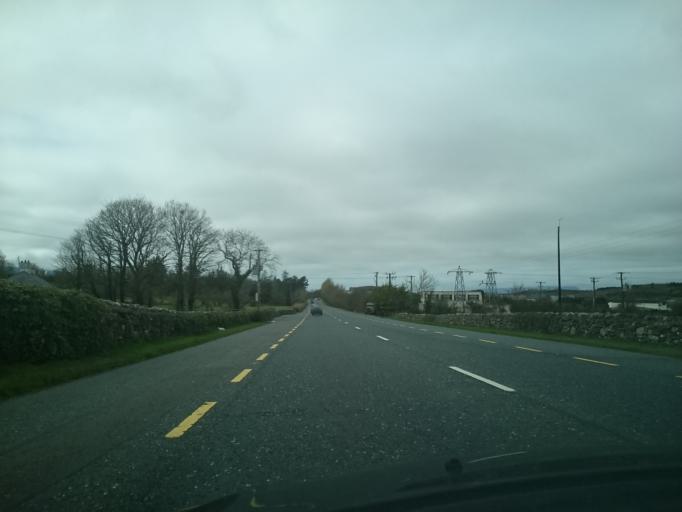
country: IE
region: Connaught
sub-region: Maigh Eo
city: Westport
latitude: 53.8036
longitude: -9.4983
